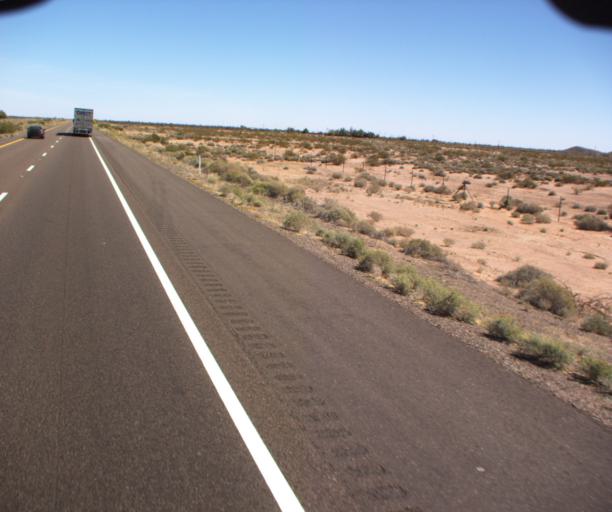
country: US
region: Arizona
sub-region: Yuma County
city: Wellton
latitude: 32.8113
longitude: -113.5123
